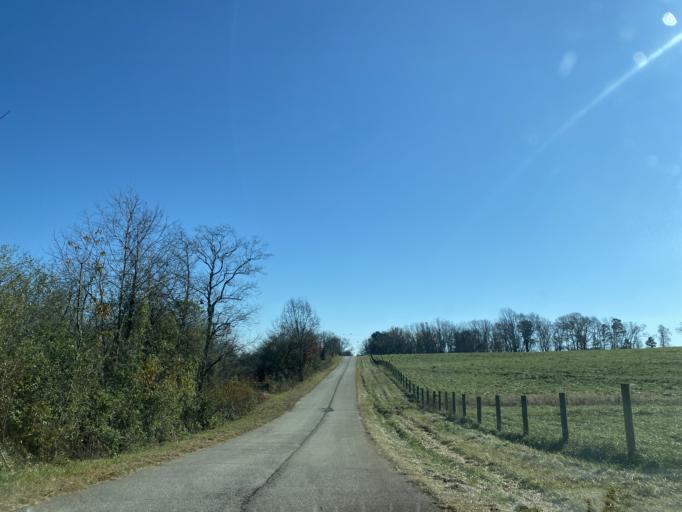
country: US
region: South Carolina
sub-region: Spartanburg County
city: Mayo
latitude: 35.1382
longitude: -81.7695
